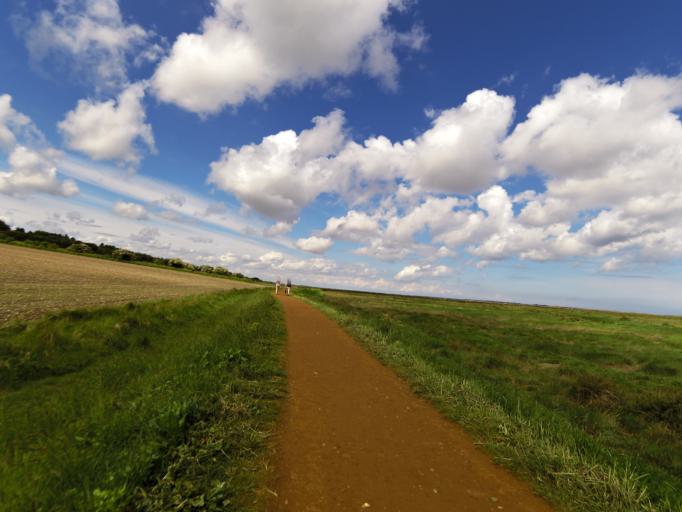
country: GB
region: England
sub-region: Norfolk
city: Briston
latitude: 52.9555
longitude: 1.0067
